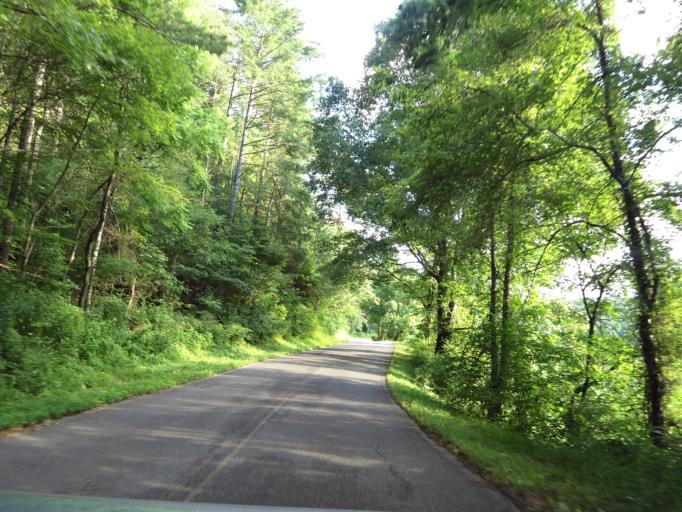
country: US
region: Tennessee
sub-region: Blount County
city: Maryville
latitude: 35.6130
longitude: -83.9434
